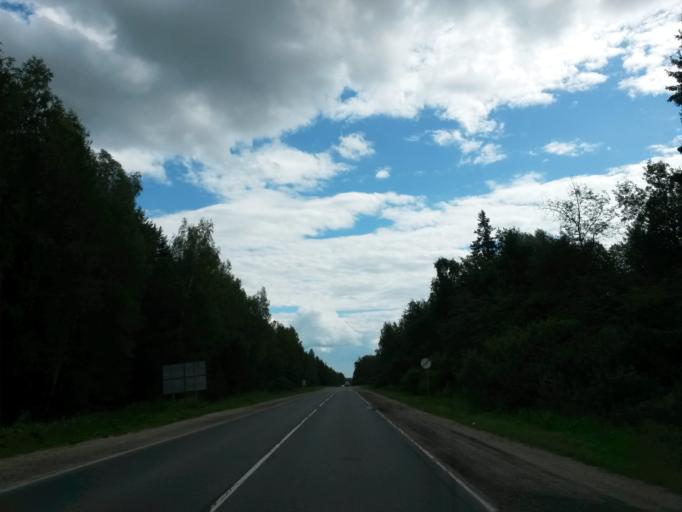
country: RU
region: Ivanovo
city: Pistsovo
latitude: 57.0774
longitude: 40.6785
